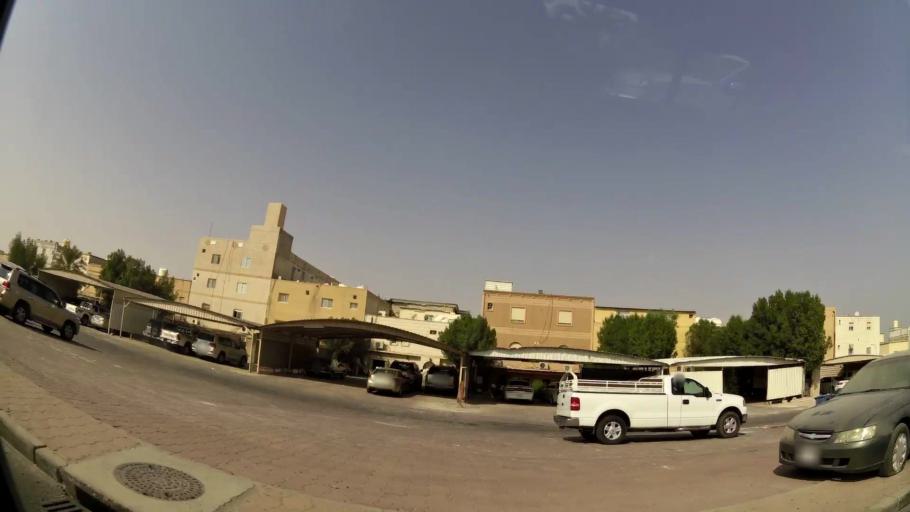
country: KW
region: Muhafazat al Jahra'
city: Al Jahra'
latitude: 29.3371
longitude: 47.6533
